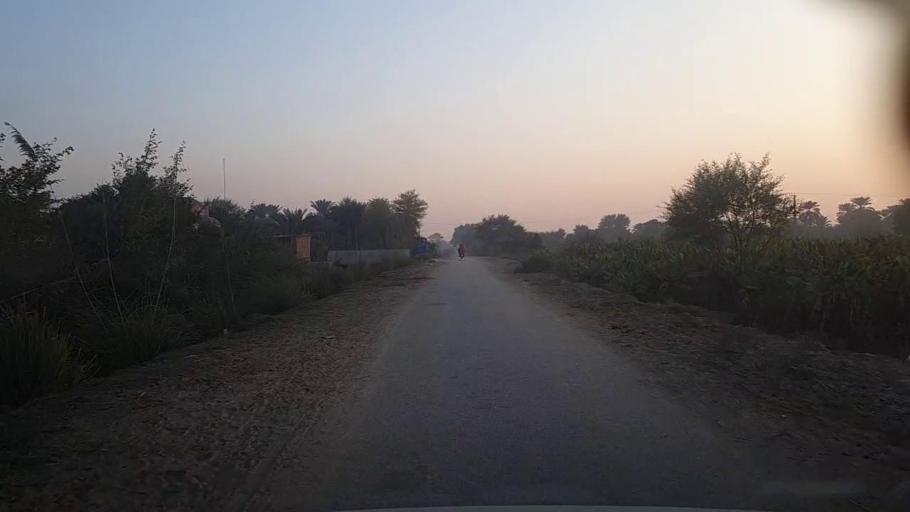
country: PK
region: Sindh
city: Karaundi
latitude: 26.8408
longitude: 68.3701
